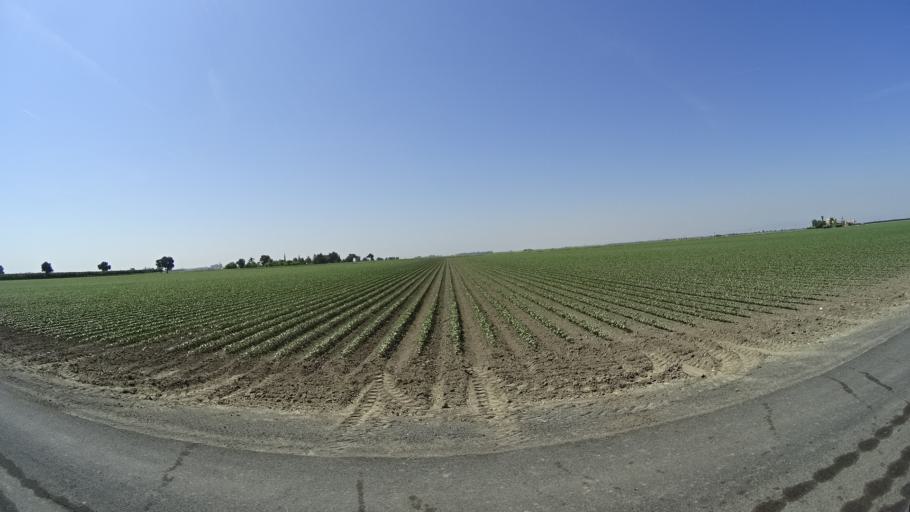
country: US
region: California
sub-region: Kings County
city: Lemoore
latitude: 36.3279
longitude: -119.8378
